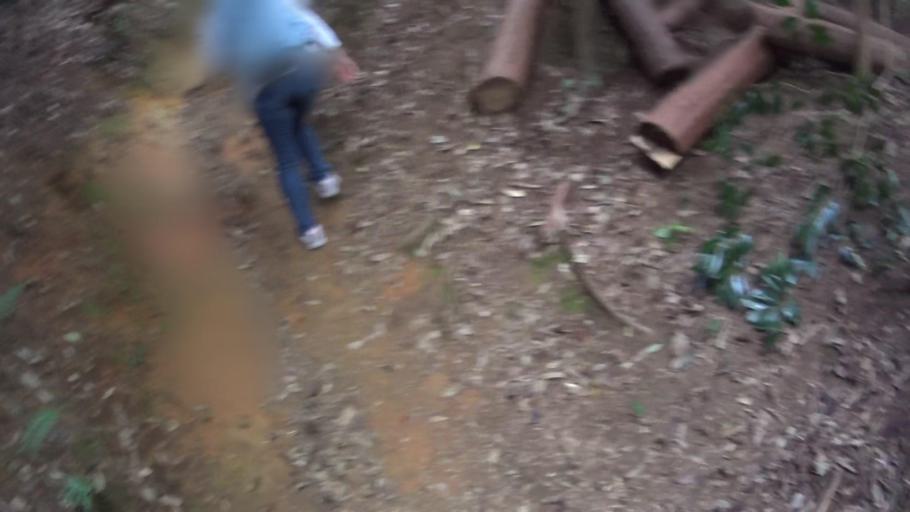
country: JP
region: Osaka
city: Kaizuka
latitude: 34.4763
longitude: 135.3089
